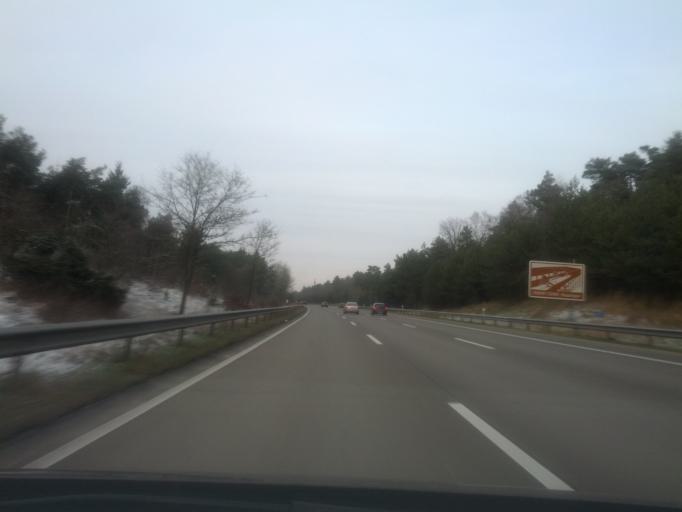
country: DE
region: Lower Saxony
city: Bispingen
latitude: 53.0417
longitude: 9.9512
